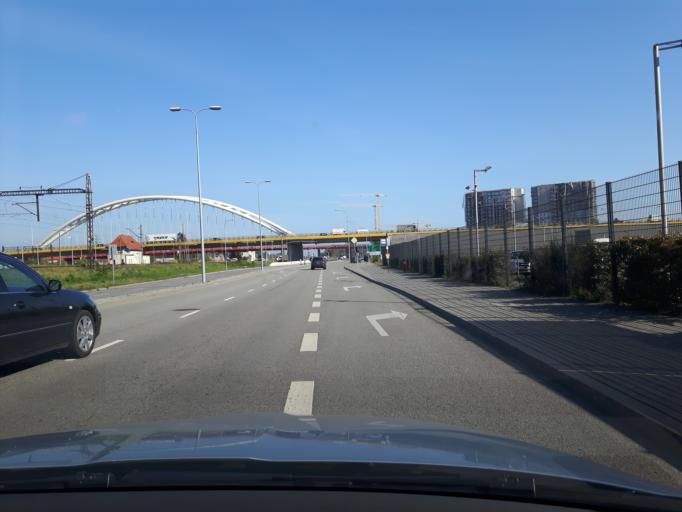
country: PL
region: Pomeranian Voivodeship
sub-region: Gdansk
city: Gdansk
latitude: 54.3914
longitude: 18.6381
